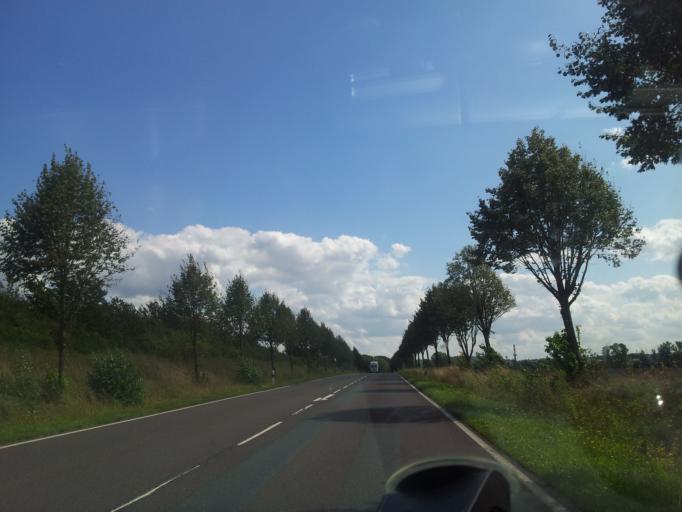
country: DE
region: Saxony-Anhalt
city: Haldensleben I
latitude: 52.2943
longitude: 11.4311
